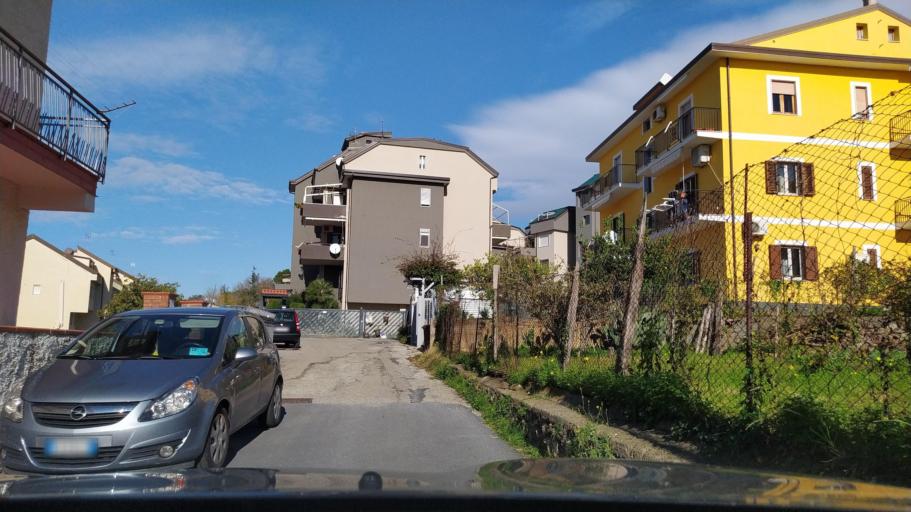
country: IT
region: Calabria
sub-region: Provincia di Cosenza
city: Paola
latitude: 39.3687
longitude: 16.0300
